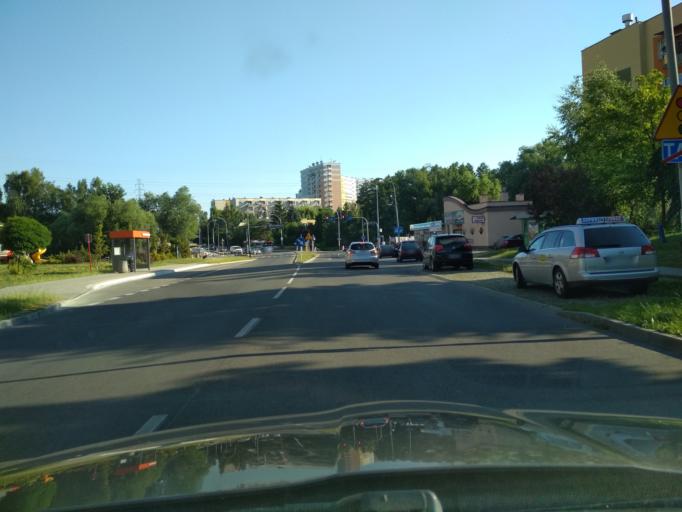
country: PL
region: Subcarpathian Voivodeship
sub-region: Rzeszow
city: Rzeszow
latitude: 50.0547
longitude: 21.9785
